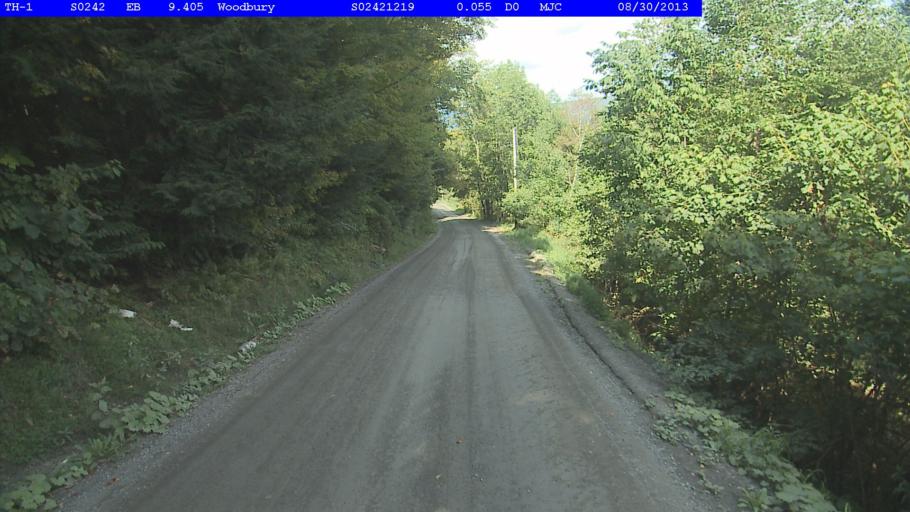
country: US
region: Vermont
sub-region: Caledonia County
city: Hardwick
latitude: 44.4040
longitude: -72.4311
